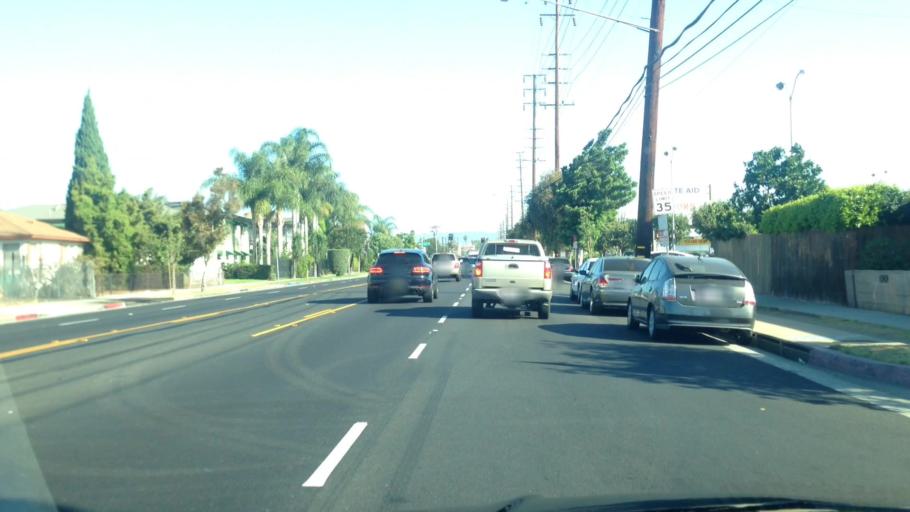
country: US
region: California
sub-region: Los Angeles County
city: Marina del Rey
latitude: 33.9976
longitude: -118.4289
